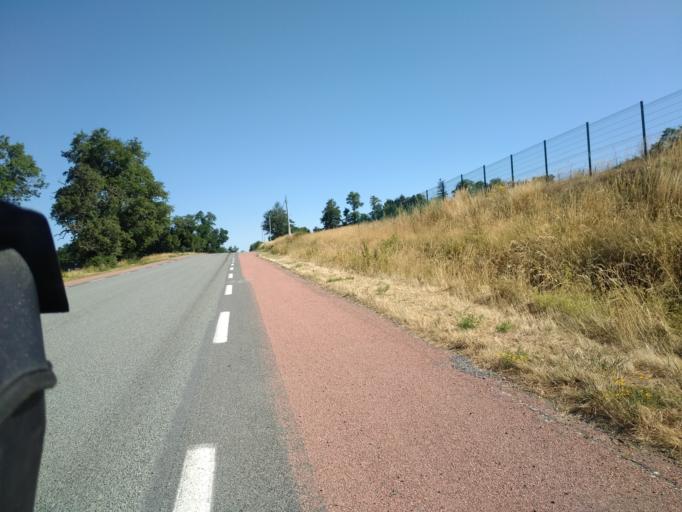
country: FR
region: Rhone-Alpes
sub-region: Departement de la Loire
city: Neulise
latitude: 45.8889
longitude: 4.1791
